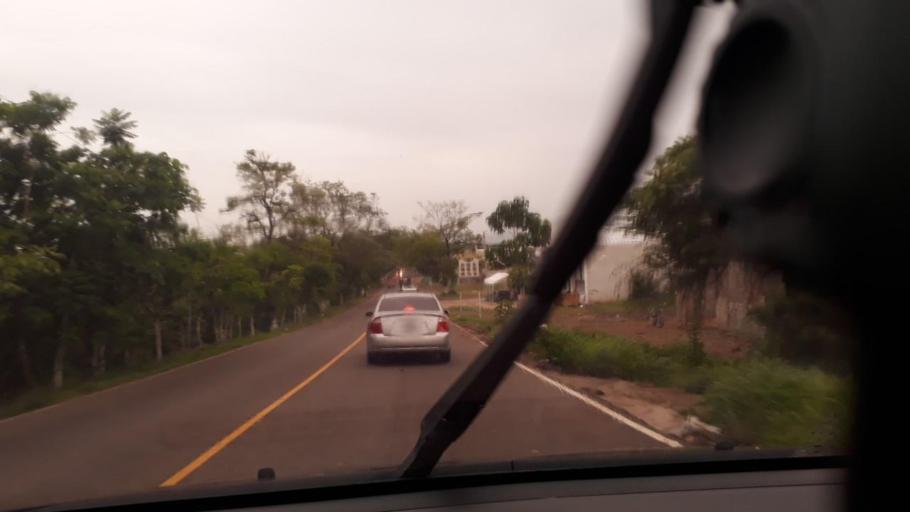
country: GT
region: Jutiapa
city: Asuncion Mita
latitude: 14.3468
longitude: -89.7150
